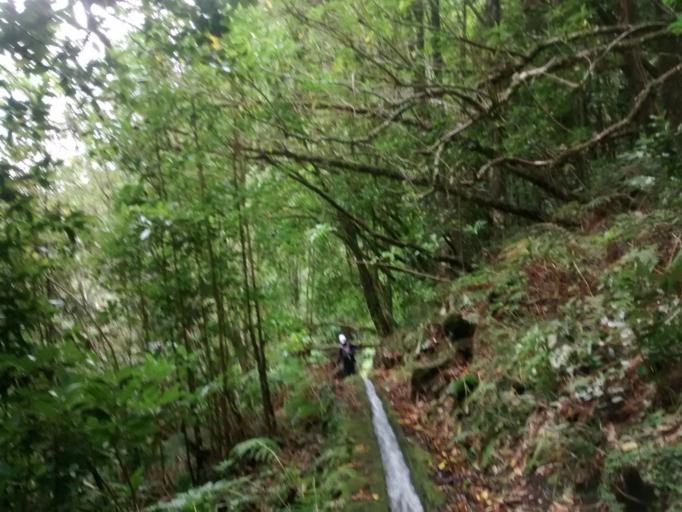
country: PT
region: Madeira
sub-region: Sao Vicente
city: Sao Vicente
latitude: 32.7563
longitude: -17.0481
